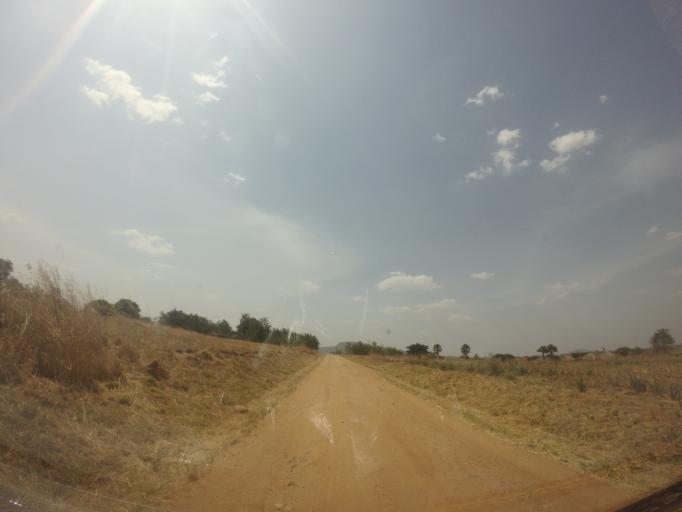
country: UG
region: Northern Region
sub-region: Arua District
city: Arua
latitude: 2.9092
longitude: 31.0535
